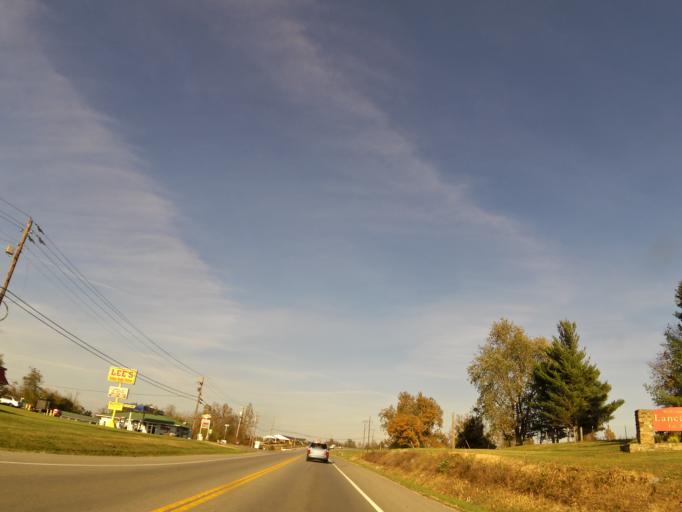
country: US
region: Kentucky
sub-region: Garrard County
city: Lancaster
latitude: 37.6015
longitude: -84.5896
